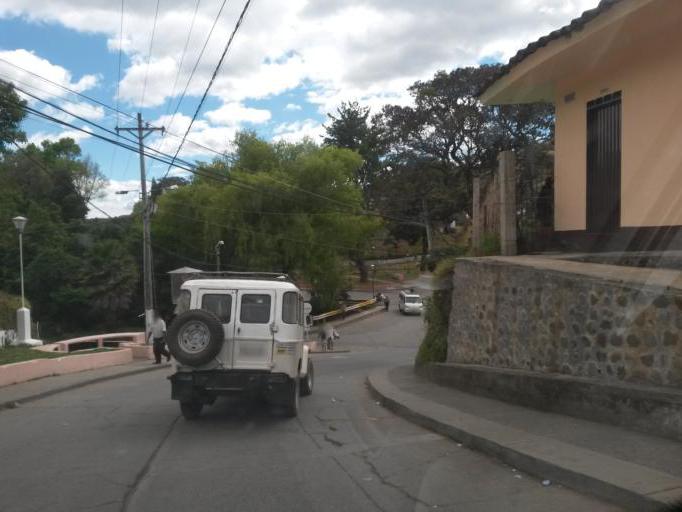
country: CO
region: Cauca
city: Silvia
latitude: 2.6107
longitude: -76.3804
